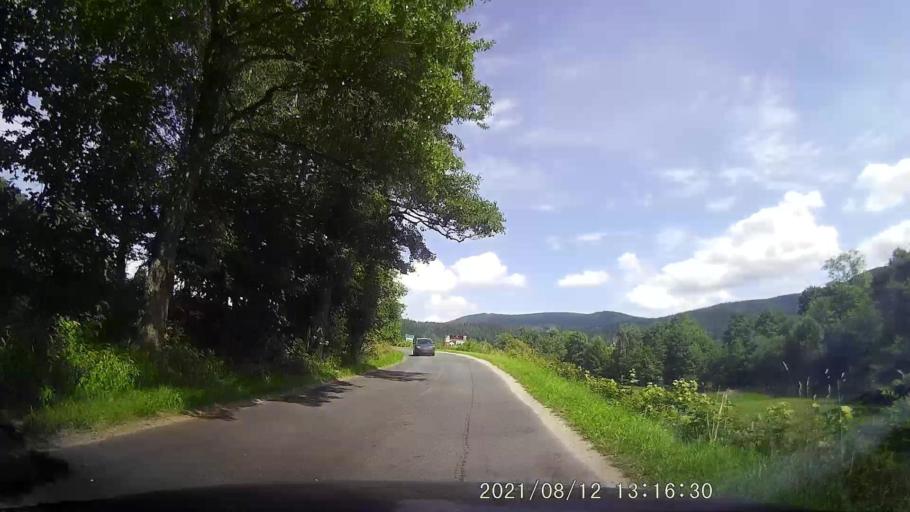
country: PL
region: Lower Silesian Voivodeship
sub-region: Powiat klodzki
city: Stronie Slaskie
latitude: 50.2643
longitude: 16.8784
